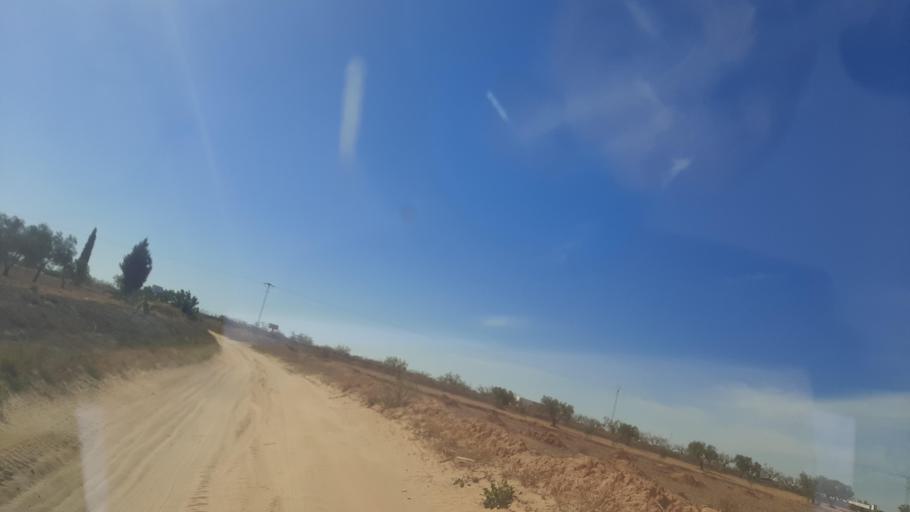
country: TN
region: Safaqis
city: Sfax
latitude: 34.8302
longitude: 10.5561
